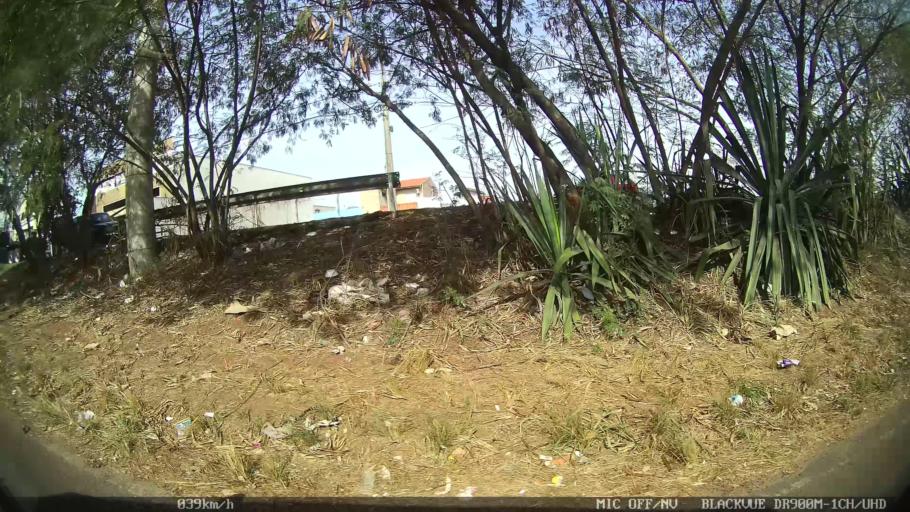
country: BR
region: Sao Paulo
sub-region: Piracicaba
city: Piracicaba
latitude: -22.6868
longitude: -47.6714
